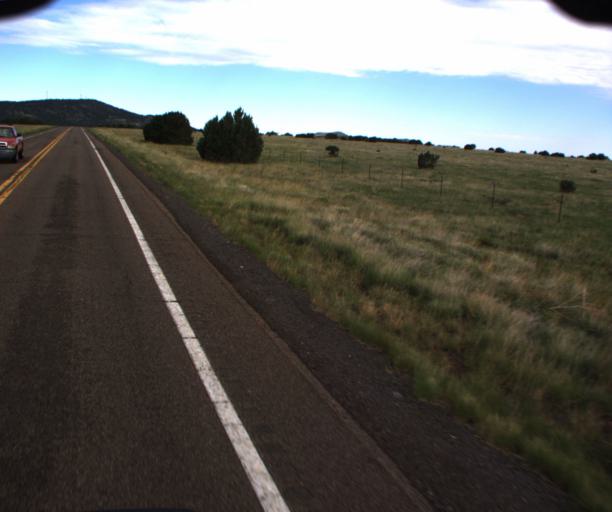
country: US
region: Arizona
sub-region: Apache County
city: Springerville
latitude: 34.2513
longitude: -109.5388
